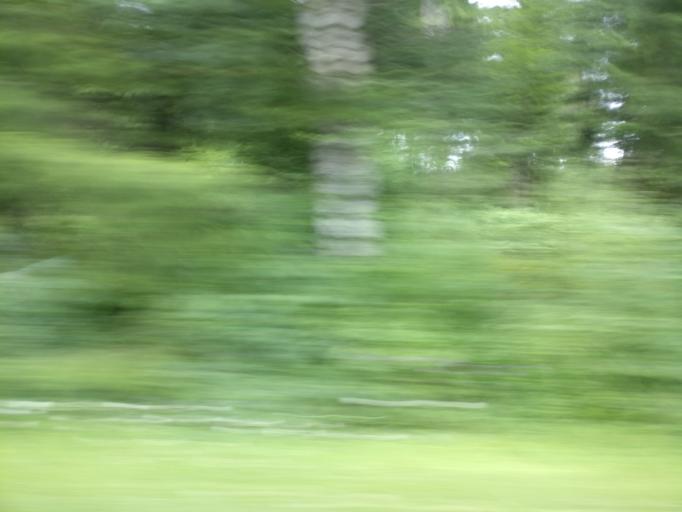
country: FI
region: Northern Savo
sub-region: Varkaus
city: Kangaslampi
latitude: 62.1606
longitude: 28.1497
